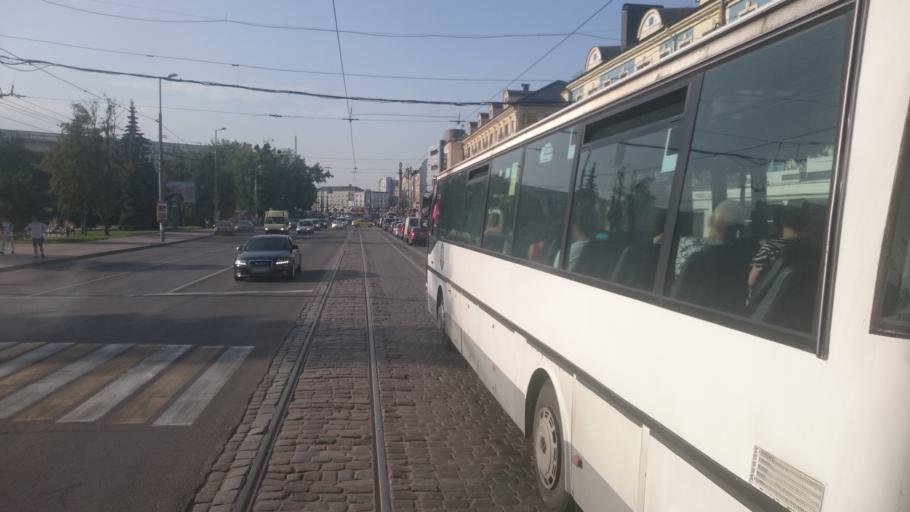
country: RU
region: Kaliningrad
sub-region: Gorod Kaliningrad
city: Kaliningrad
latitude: 54.7165
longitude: 20.5029
